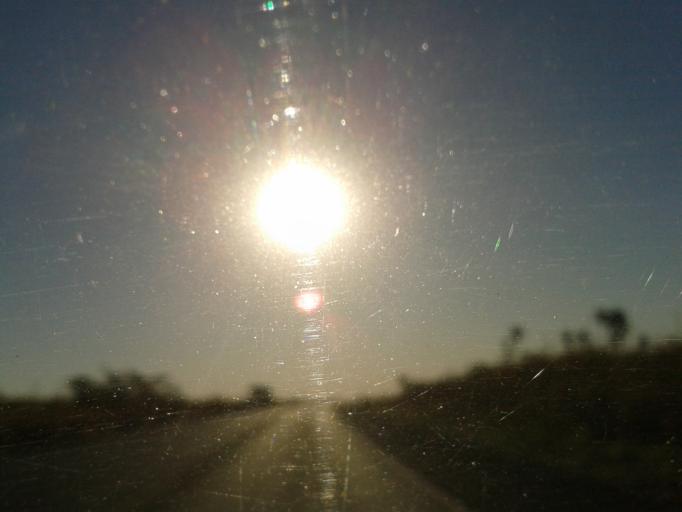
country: BR
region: Minas Gerais
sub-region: Santa Vitoria
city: Santa Vitoria
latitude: -19.1189
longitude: -50.3060
